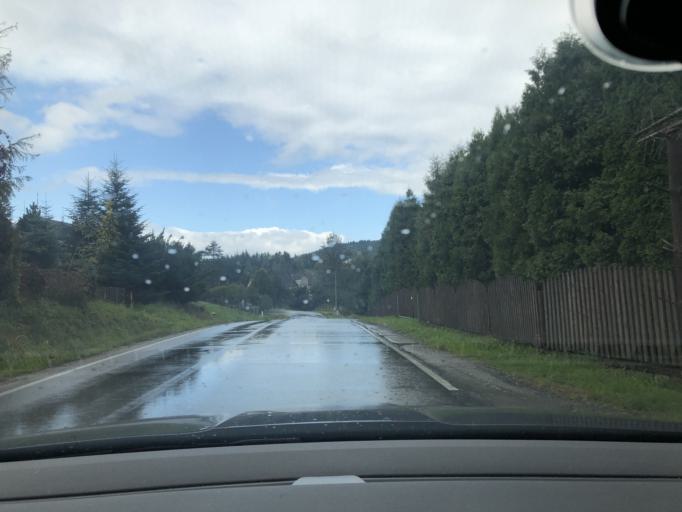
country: PL
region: Lesser Poland Voivodeship
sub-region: Powiat suski
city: Zawoja
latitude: 49.6846
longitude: 19.5657
